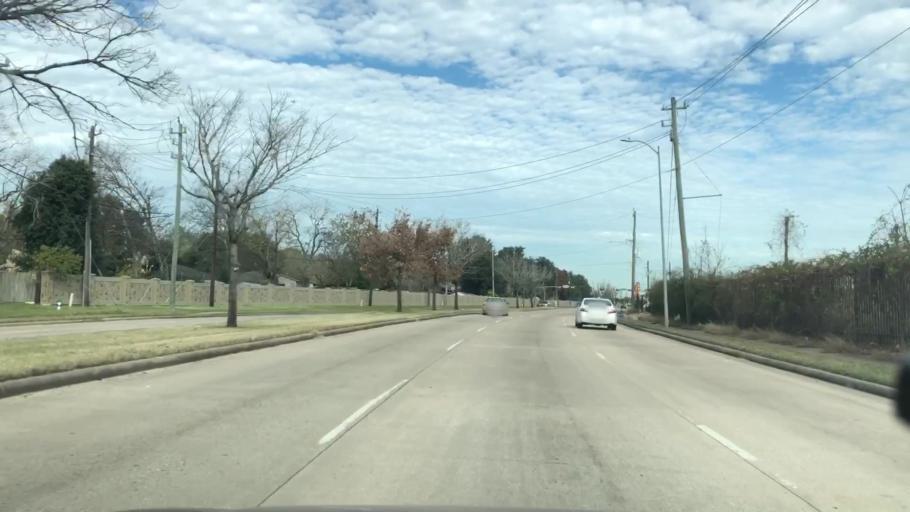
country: US
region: Texas
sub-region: Fort Bend County
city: Missouri City
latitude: 29.6322
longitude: -95.5080
